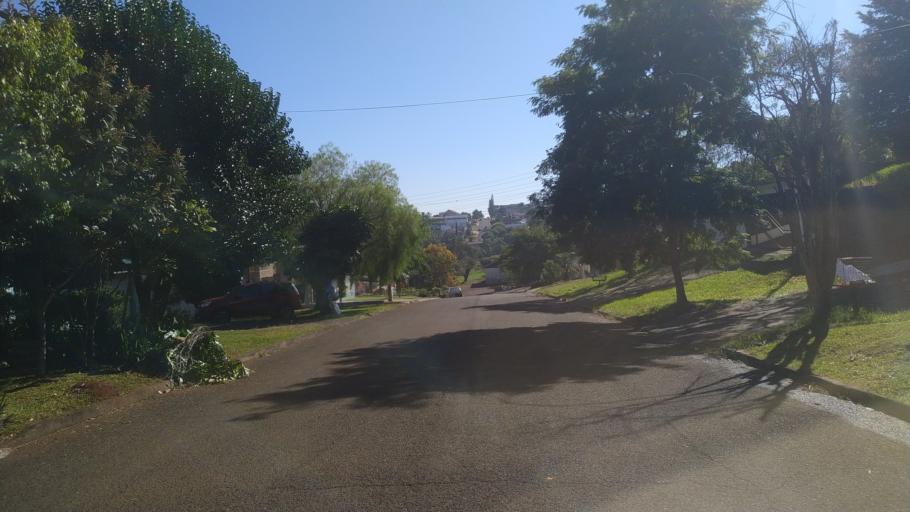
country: BR
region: Santa Catarina
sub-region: Chapeco
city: Chapeco
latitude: -27.1100
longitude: -52.6017
